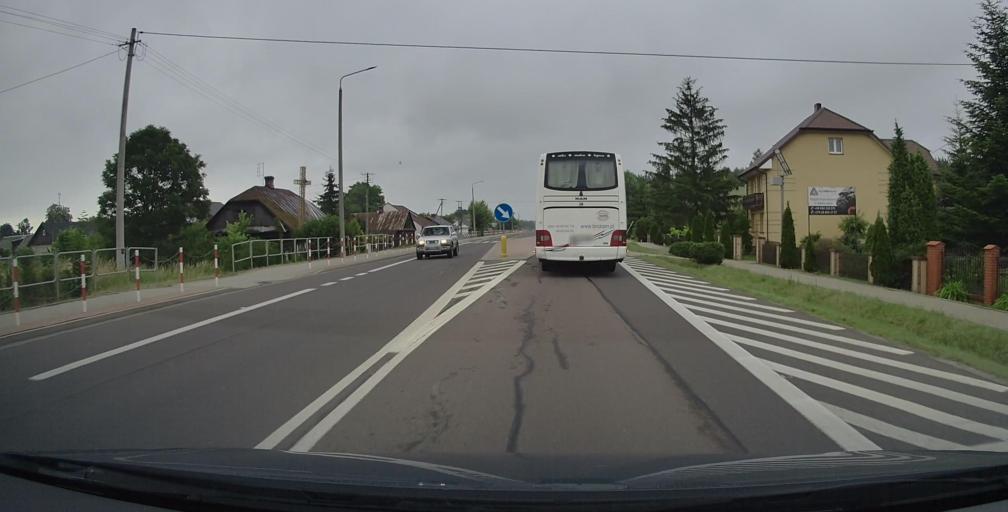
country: PL
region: Lublin Voivodeship
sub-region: Powiat bialski
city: Terespol
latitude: 52.0397
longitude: 23.5125
